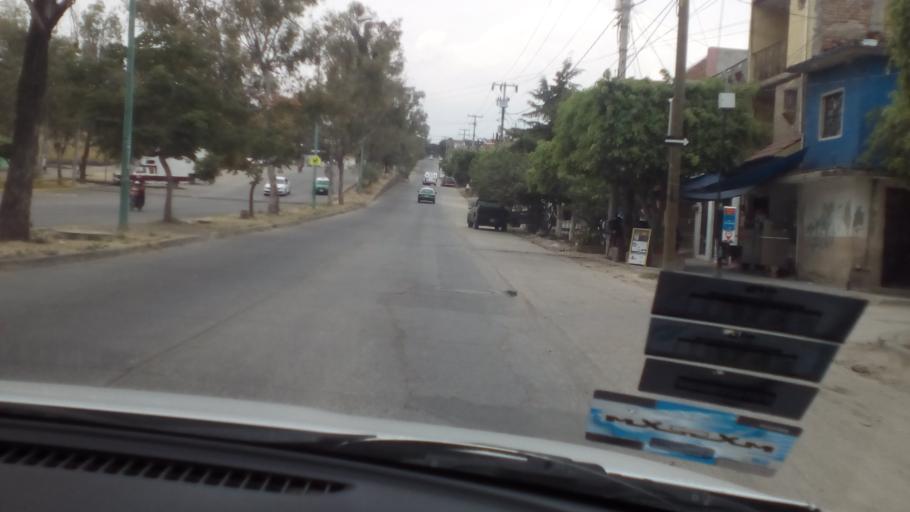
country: MX
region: Guanajuato
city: Leon
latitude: 21.1266
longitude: -101.6995
